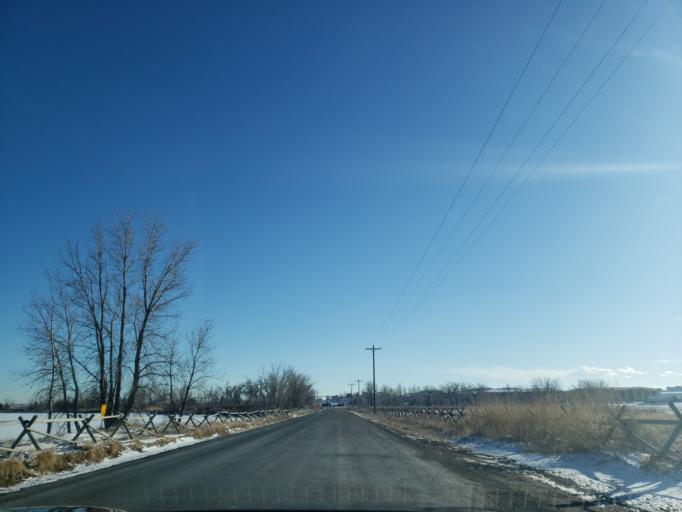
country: US
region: Colorado
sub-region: Larimer County
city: Fort Collins
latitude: 40.5268
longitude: -105.0013
